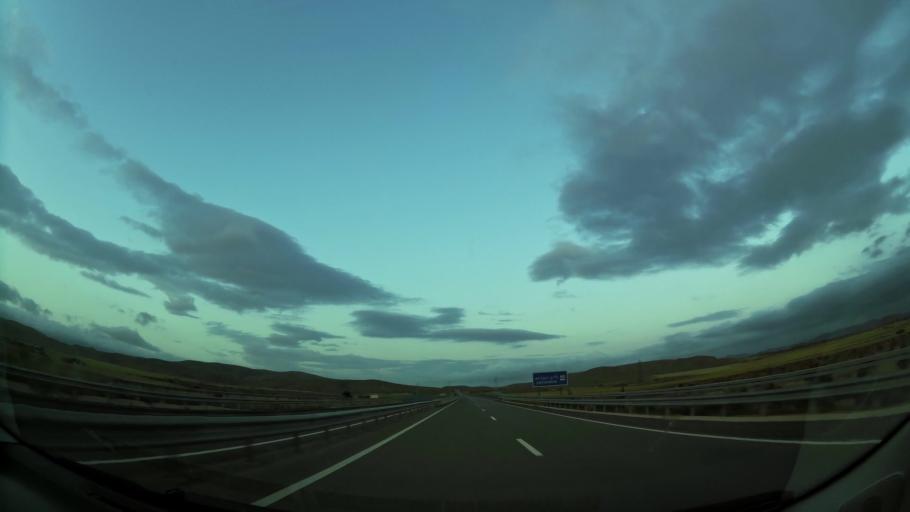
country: MA
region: Oriental
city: El Aioun
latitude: 34.6047
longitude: -2.6129
